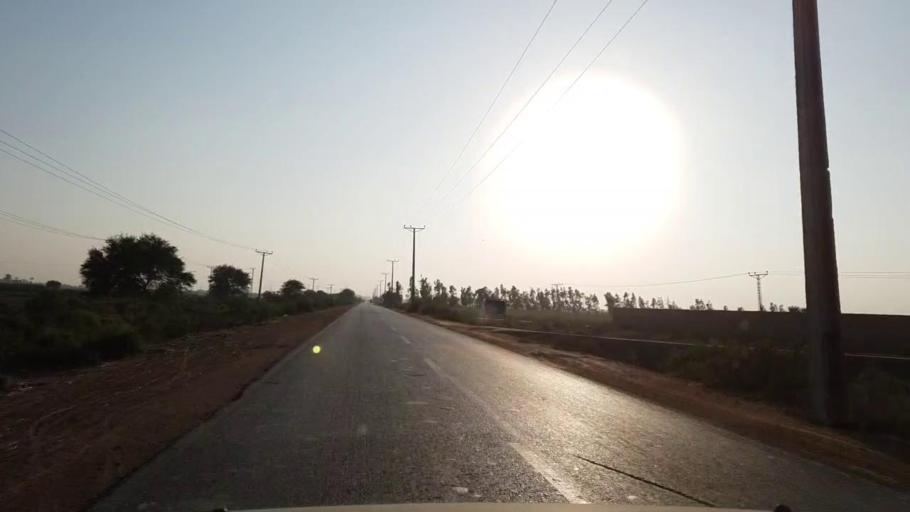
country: PK
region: Sindh
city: Daro Mehar
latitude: 24.6253
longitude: 68.0995
